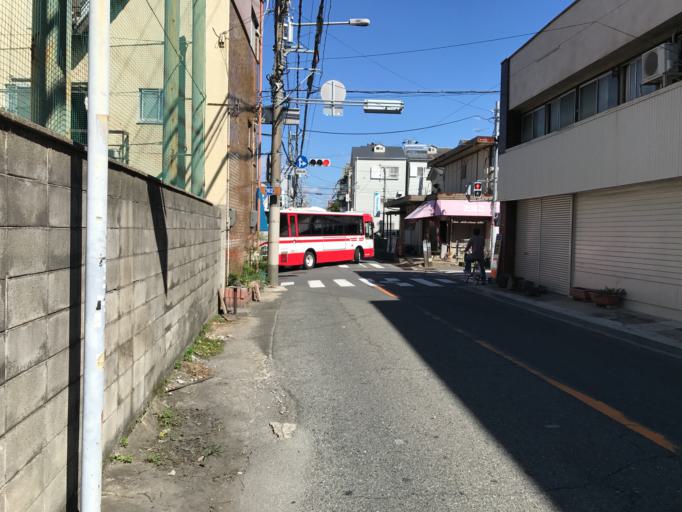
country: JP
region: Osaka
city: Daitocho
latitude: 34.7322
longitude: 135.6417
